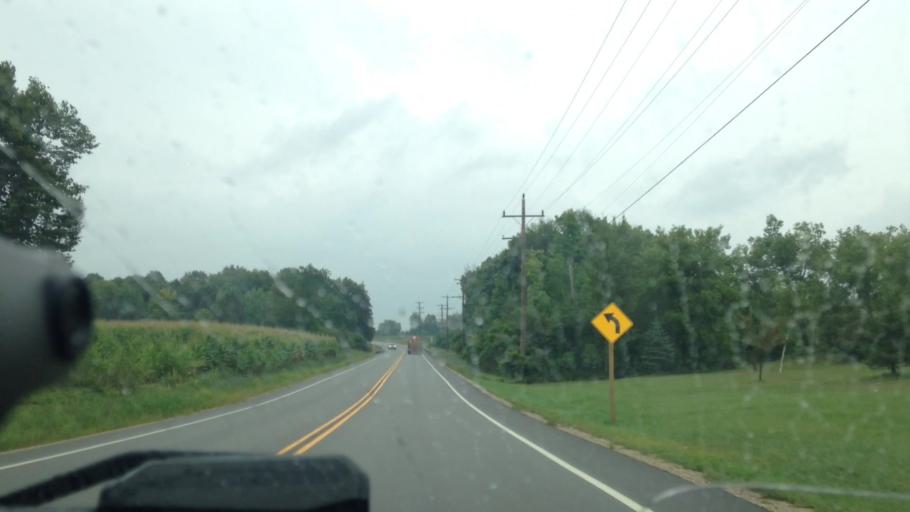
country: US
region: Wisconsin
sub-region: Washington County
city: Slinger
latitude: 43.3175
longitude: -88.2660
